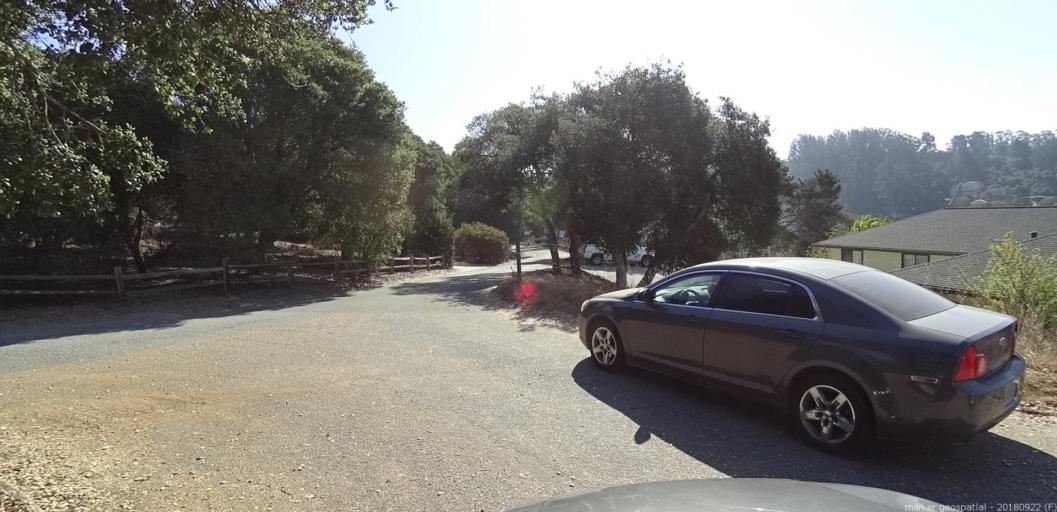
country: US
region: California
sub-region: Monterey County
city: Prunedale
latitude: 36.8049
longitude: -121.6576
